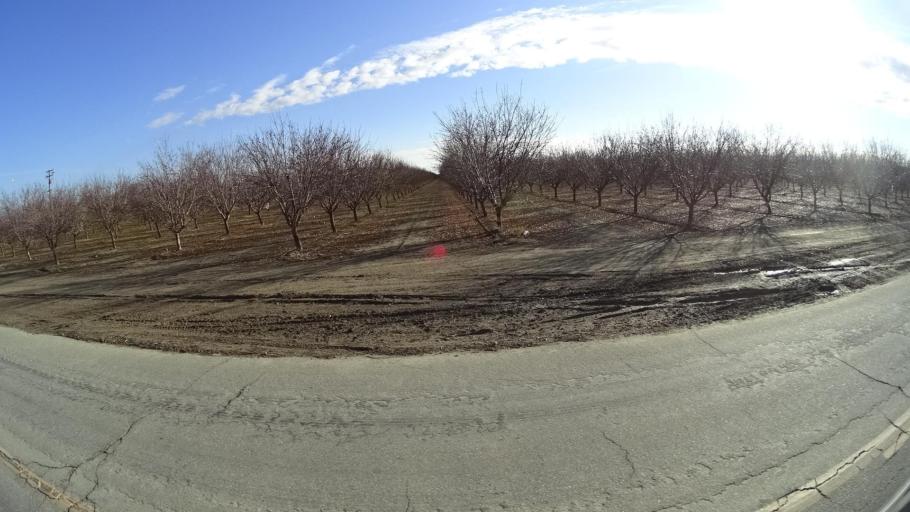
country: US
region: California
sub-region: Kern County
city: Delano
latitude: 35.7606
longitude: -119.3298
